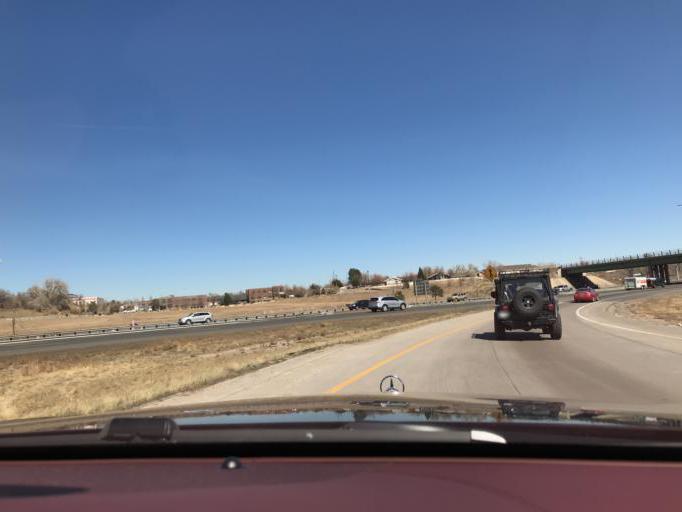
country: US
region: Colorado
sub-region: Jefferson County
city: Applewood
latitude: 39.7809
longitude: -105.1323
